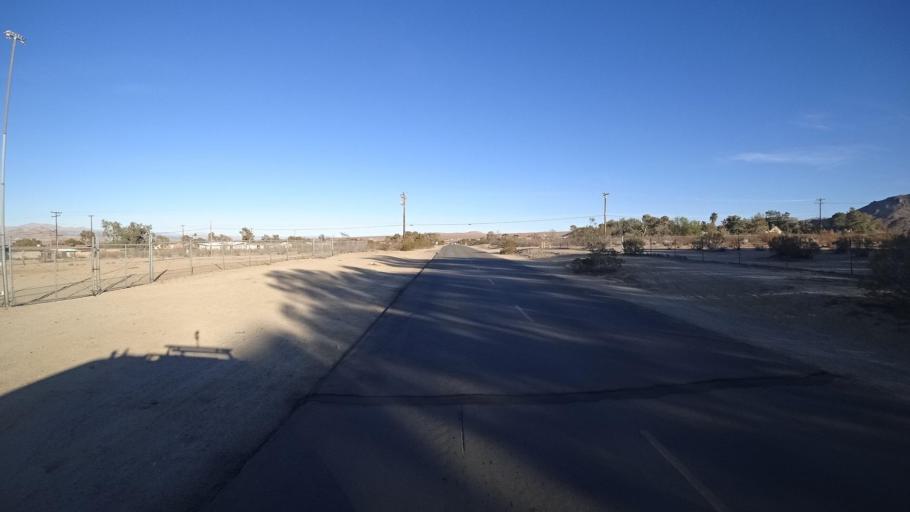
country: US
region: California
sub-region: Kern County
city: Ridgecrest
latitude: 35.5861
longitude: -117.6665
